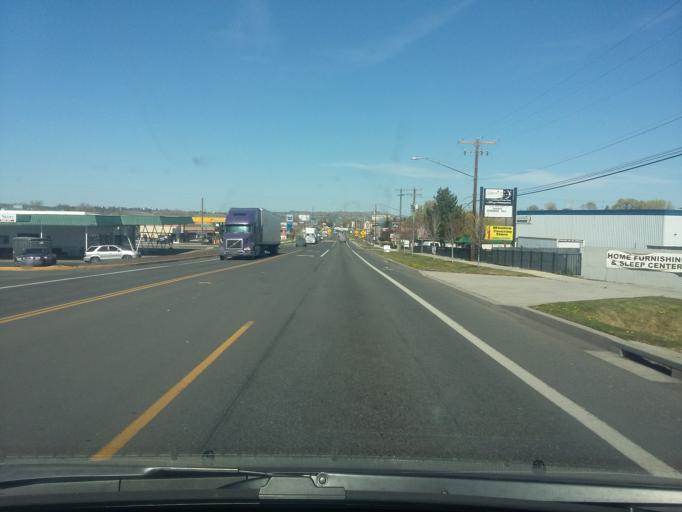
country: US
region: Oregon
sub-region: Jefferson County
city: Madras
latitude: 44.6169
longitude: -121.1341
